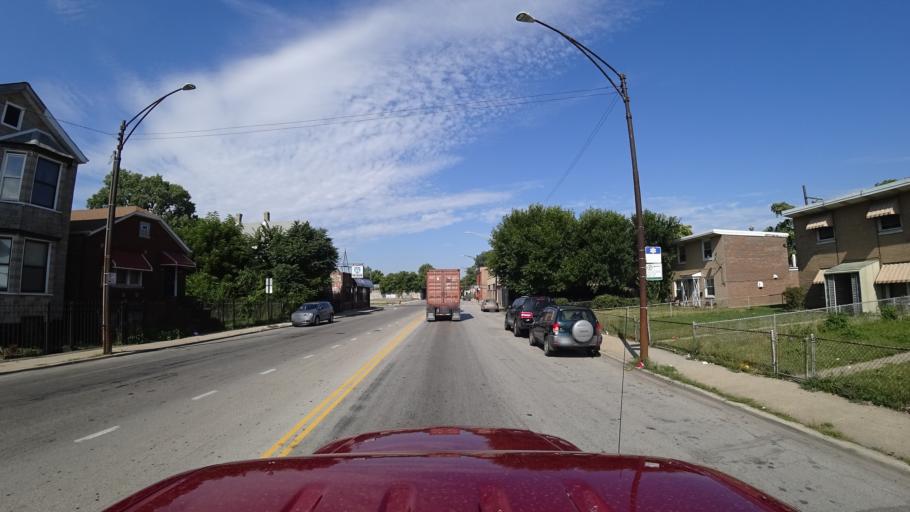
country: US
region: Illinois
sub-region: Cook County
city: Chicago
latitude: 41.8091
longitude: -87.6338
